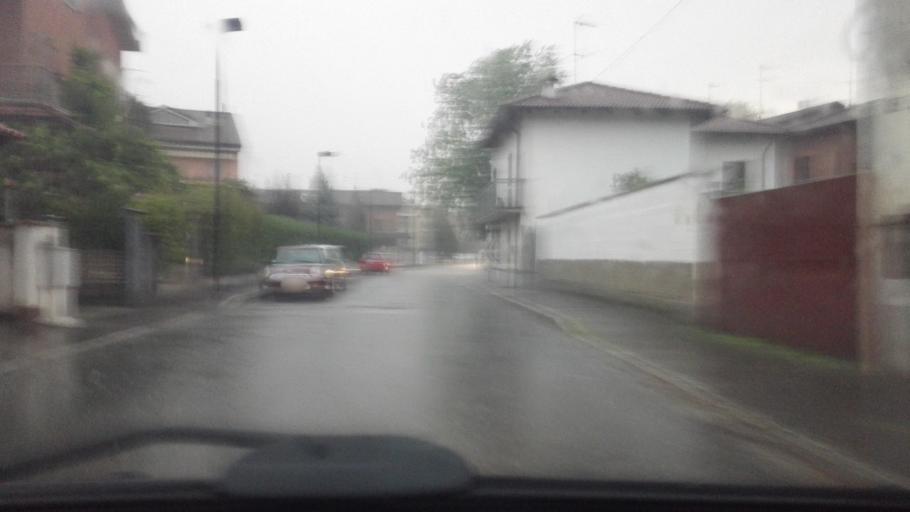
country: IT
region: Piedmont
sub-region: Provincia di Alessandria
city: Alessandria
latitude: 44.9306
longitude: 8.6201
